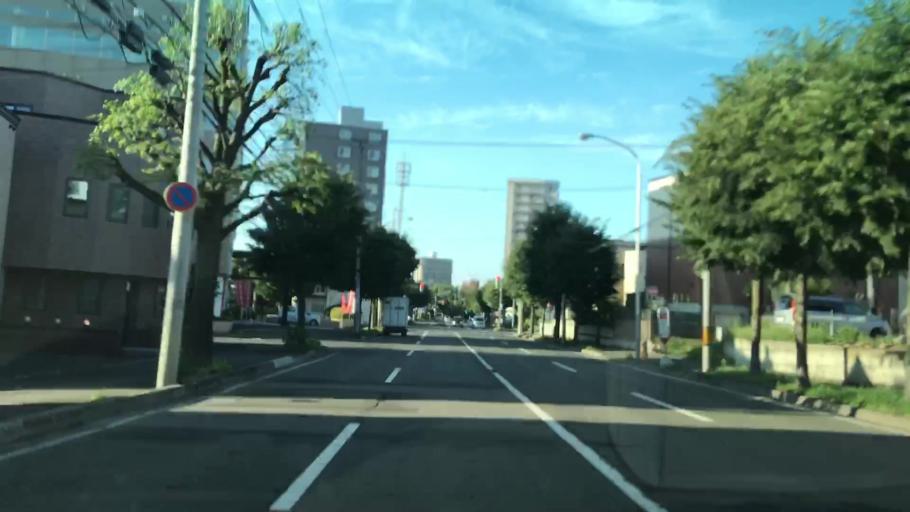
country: JP
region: Hokkaido
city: Sapporo
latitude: 43.0436
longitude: 141.3639
